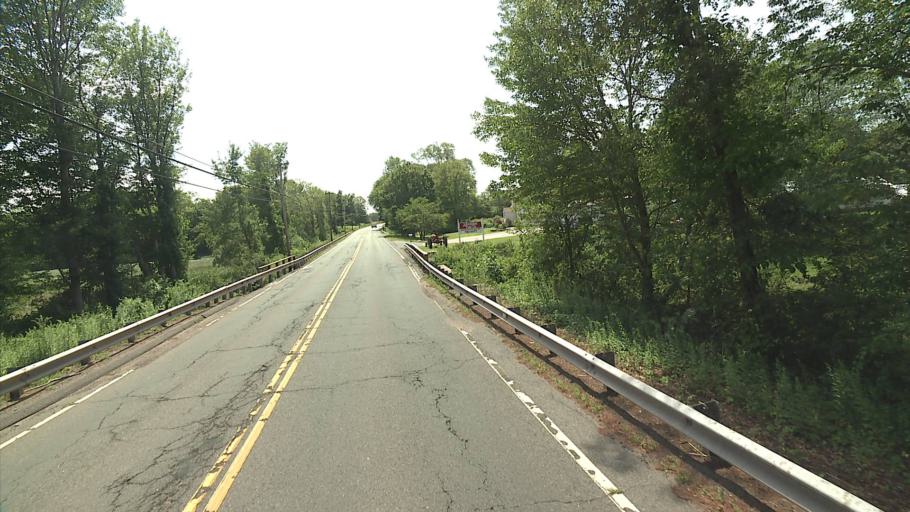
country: US
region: Connecticut
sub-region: Tolland County
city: South Coventry
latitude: 41.7591
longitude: -72.2764
